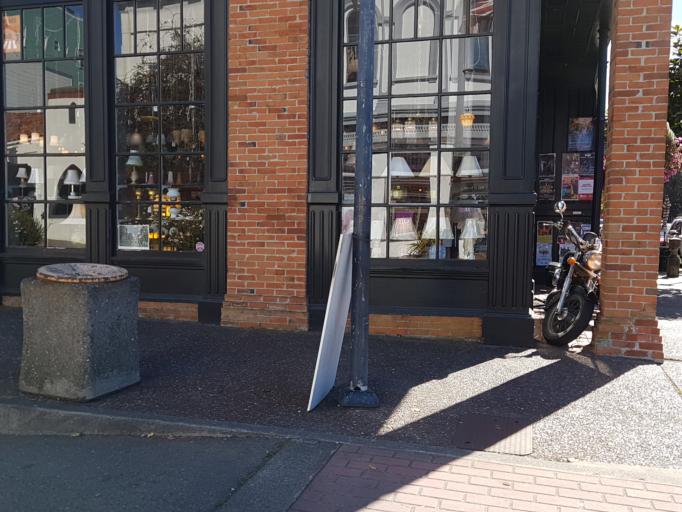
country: US
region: California
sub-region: Humboldt County
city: Eureka
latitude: 40.8044
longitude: -124.1665
